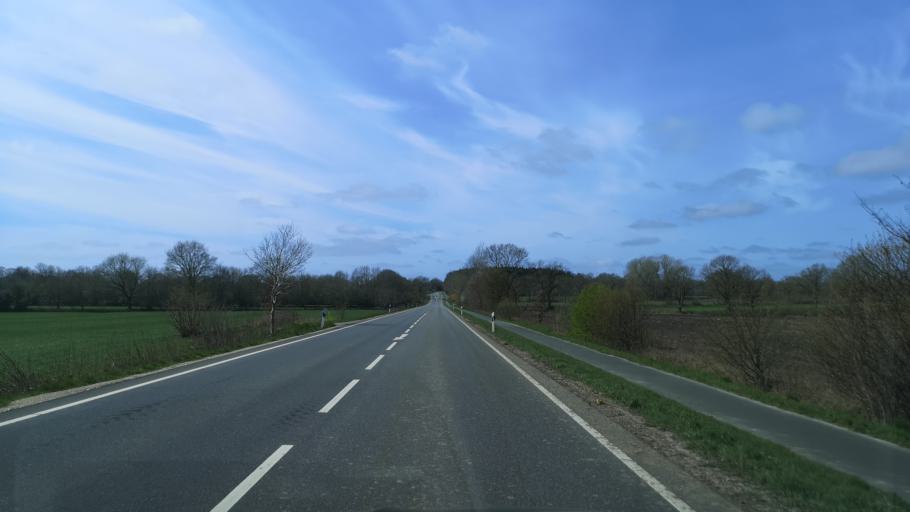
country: DE
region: Schleswig-Holstein
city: Wrohm
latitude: 54.2172
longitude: 9.3918
